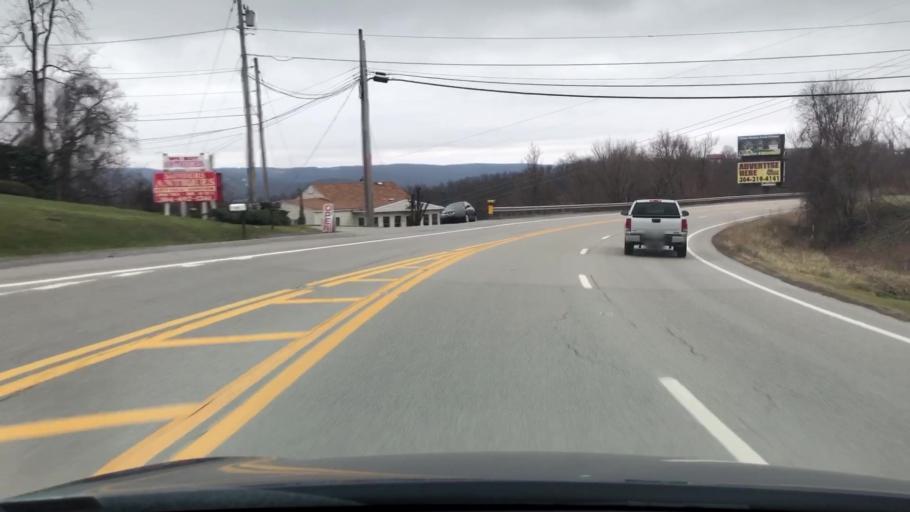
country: US
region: West Virginia
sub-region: Monongalia County
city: Morgantown
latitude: 39.5935
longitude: -79.9538
